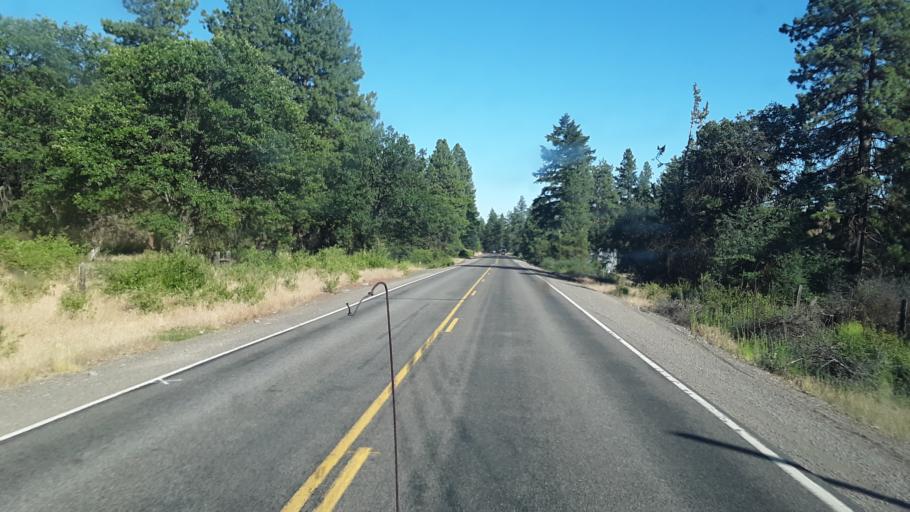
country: US
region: Oregon
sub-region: Klamath County
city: Klamath Falls
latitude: 42.2791
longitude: -121.9124
